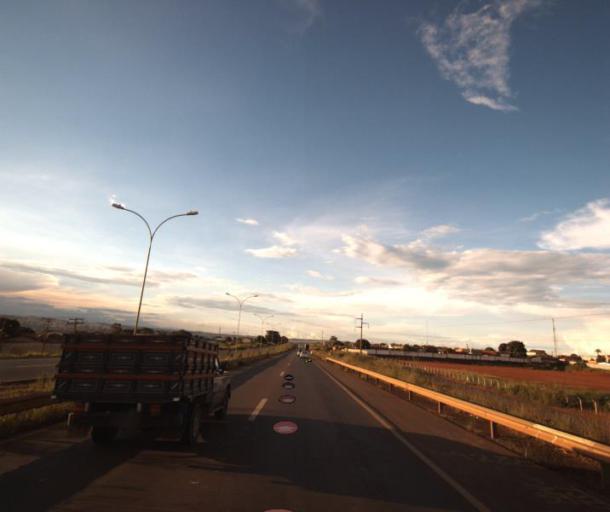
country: BR
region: Goias
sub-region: Anapolis
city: Anapolis
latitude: -16.3371
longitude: -48.9226
